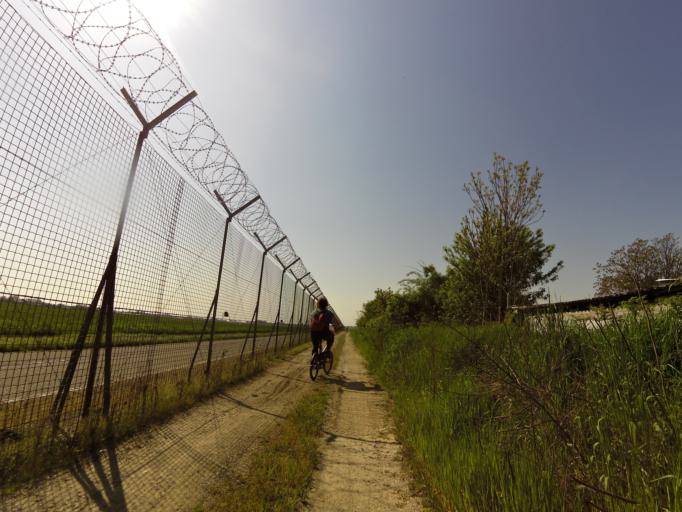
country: IT
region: Lombardy
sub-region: Citta metropolitana di Milano
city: Linate
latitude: 45.4464
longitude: 9.2747
